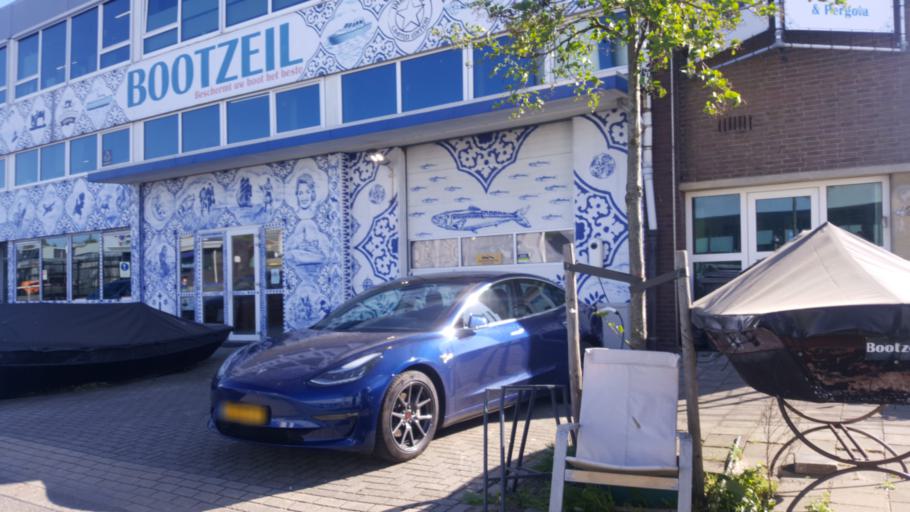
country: NL
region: North Holland
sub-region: Gemeente Haarlem
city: Haarlem
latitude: 52.3877
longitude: 4.6561
